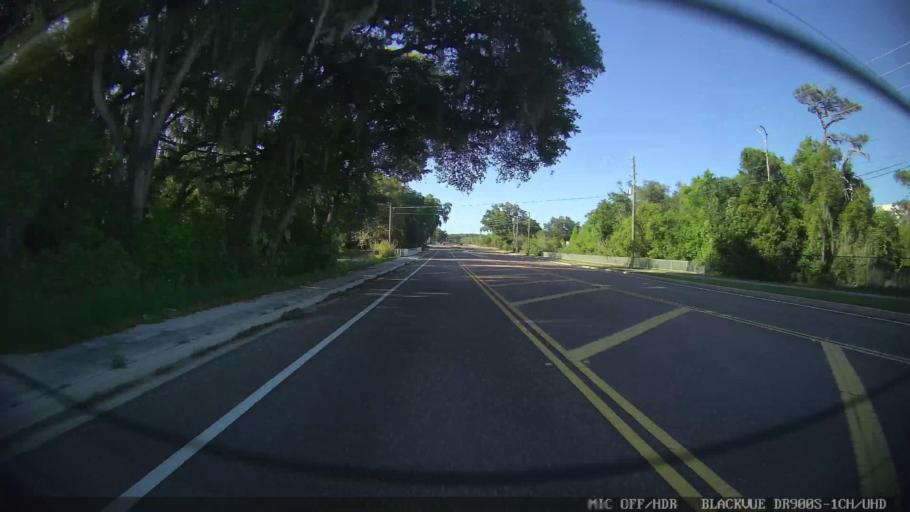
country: US
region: Florida
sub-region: Hillsborough County
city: Apollo Beach
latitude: 27.7863
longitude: -82.3474
